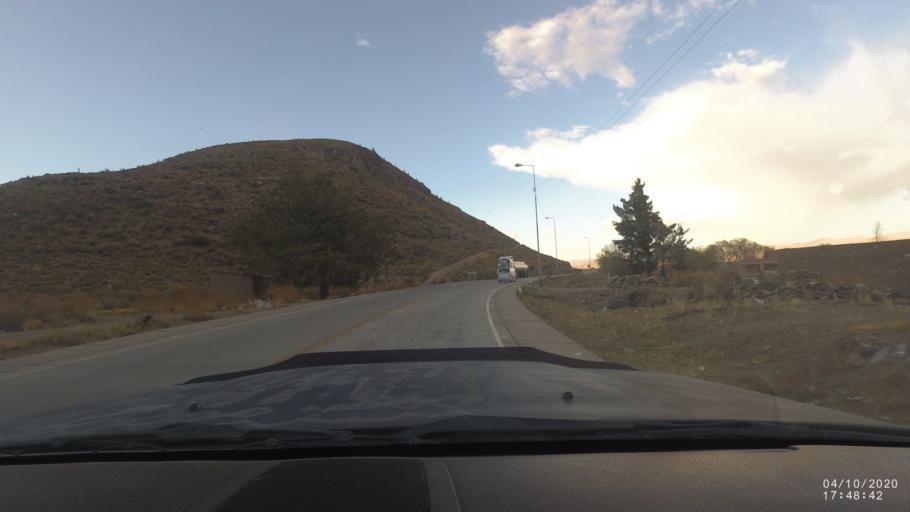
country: BO
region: Oruro
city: Oruro
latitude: -18.0152
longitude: -67.1394
